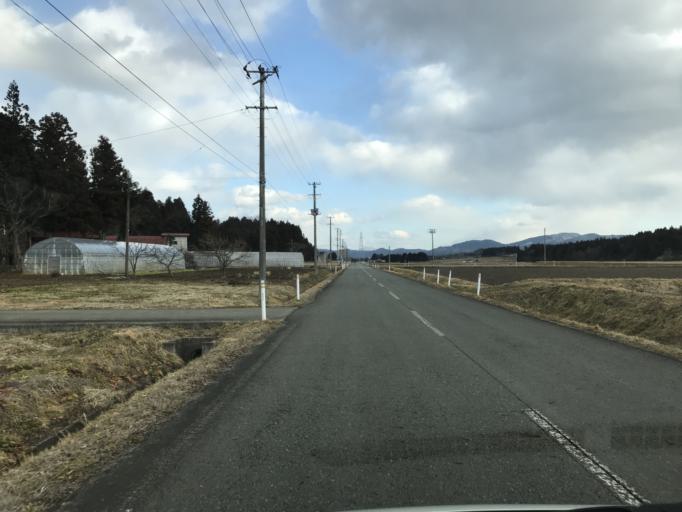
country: JP
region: Iwate
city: Mizusawa
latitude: 39.0790
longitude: 141.0777
